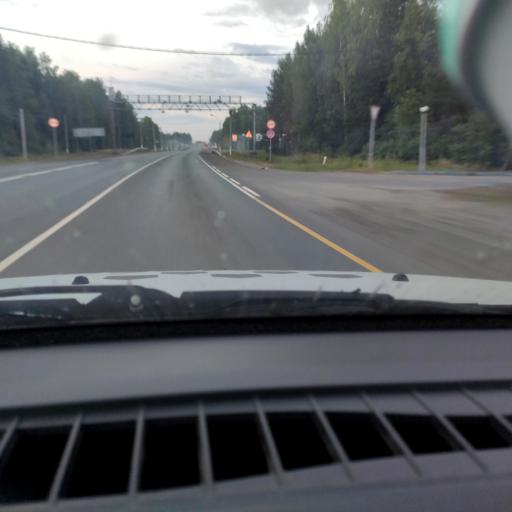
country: RU
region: Kirov
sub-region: Kirovo-Chepetskiy Rayon
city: Kirov
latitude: 58.6841
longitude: 49.6410
